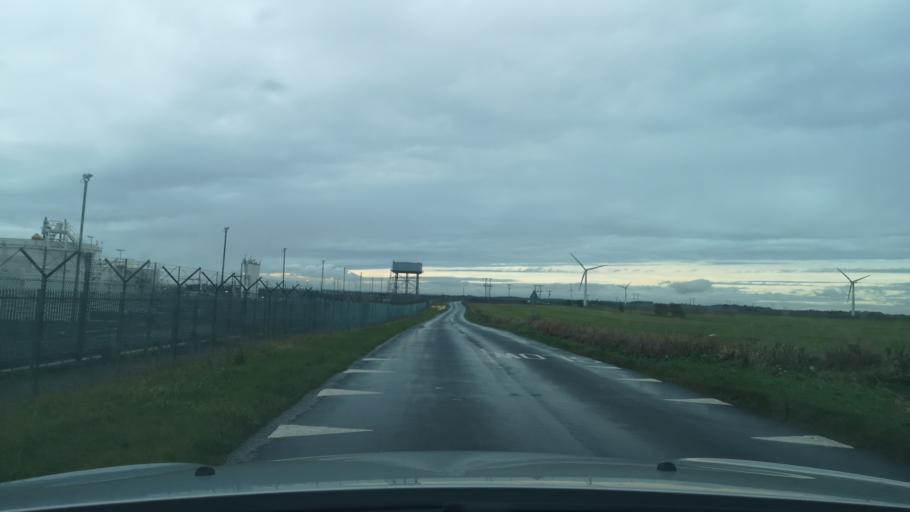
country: GB
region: England
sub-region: East Riding of Yorkshire
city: Easington
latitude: 53.6632
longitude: 0.1113
